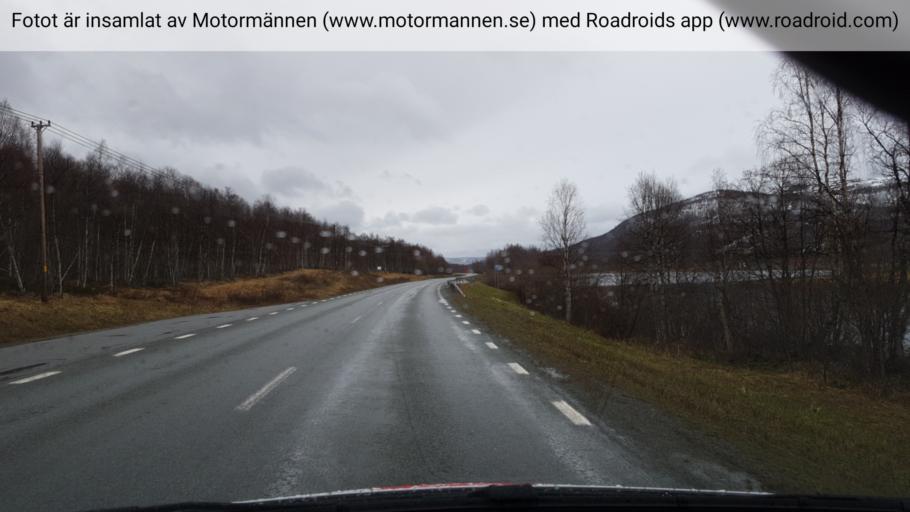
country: NO
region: Nordland
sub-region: Rana
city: Mo i Rana
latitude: 65.7982
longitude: 15.0976
